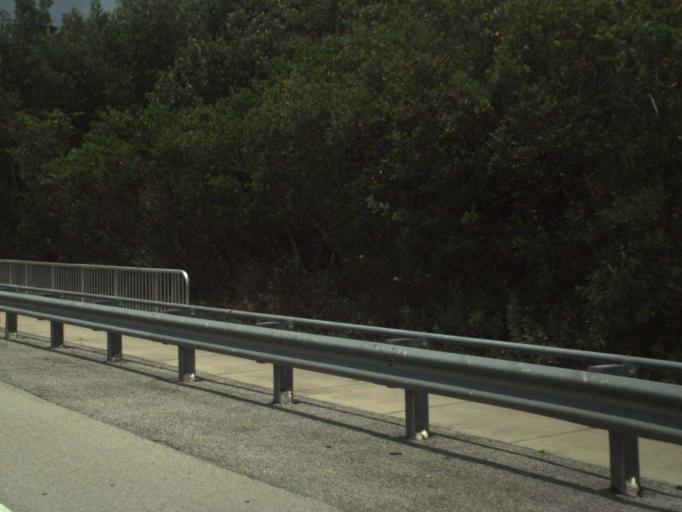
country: US
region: Florida
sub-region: Saint Lucie County
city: Indian River Estates
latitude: 27.3808
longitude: -80.2567
